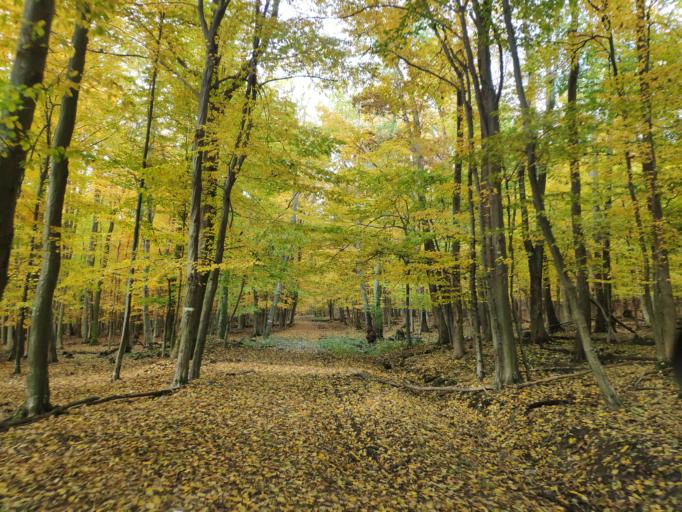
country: SK
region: Kosicky
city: Moldava nad Bodvou
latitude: 48.7193
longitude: 21.0166
